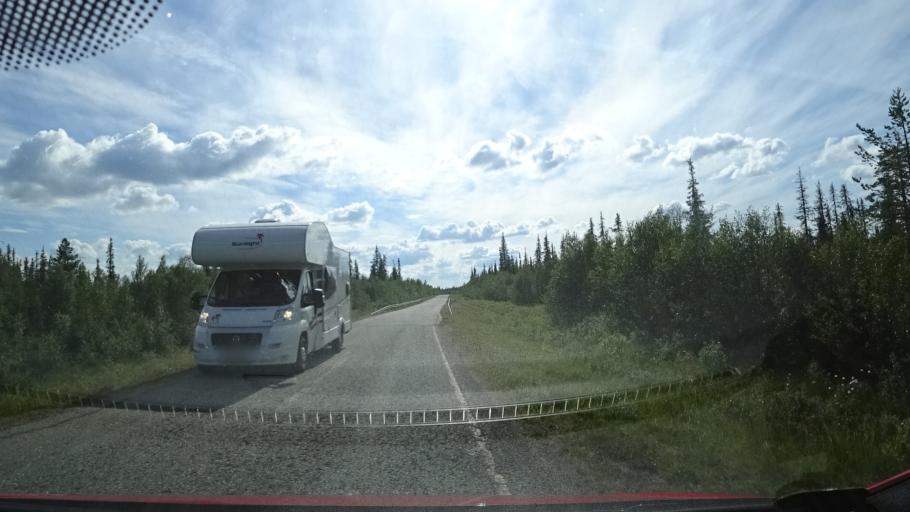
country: FI
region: Lapland
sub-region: Tunturi-Lappi
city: Kittilae
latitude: 68.2198
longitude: 25.8089
